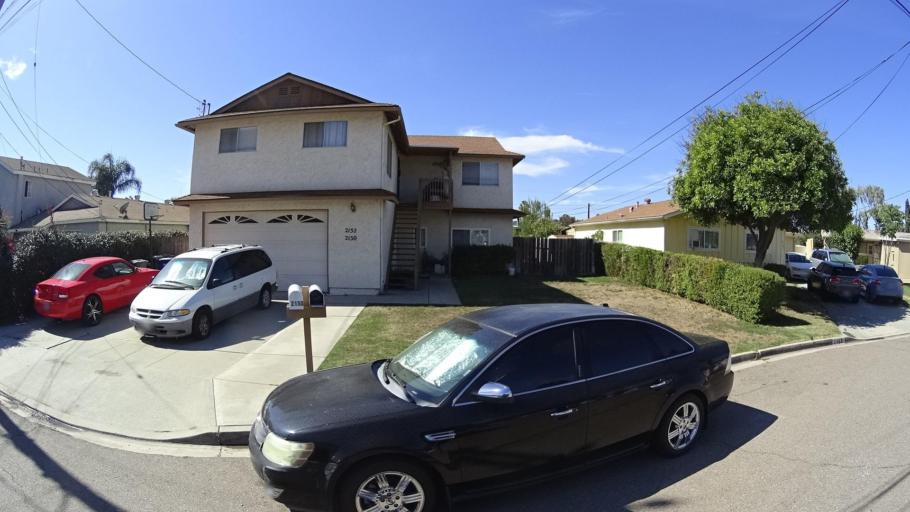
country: US
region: California
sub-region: San Diego County
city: Spring Valley
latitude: 32.7285
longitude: -117.0075
